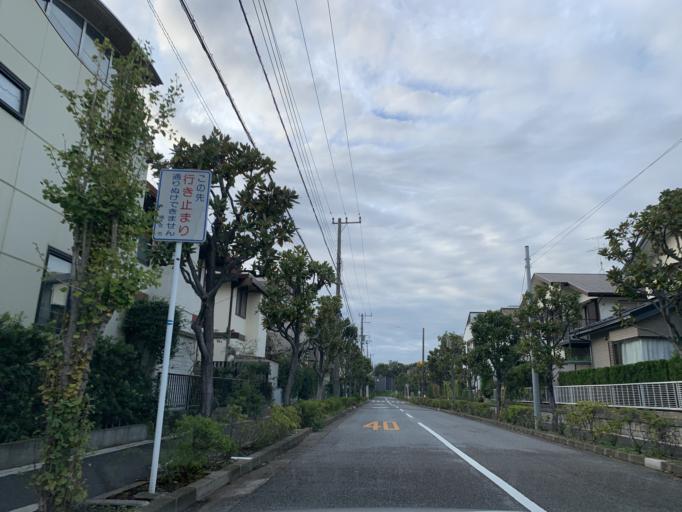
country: JP
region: Tokyo
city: Urayasu
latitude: 35.6554
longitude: 139.9133
